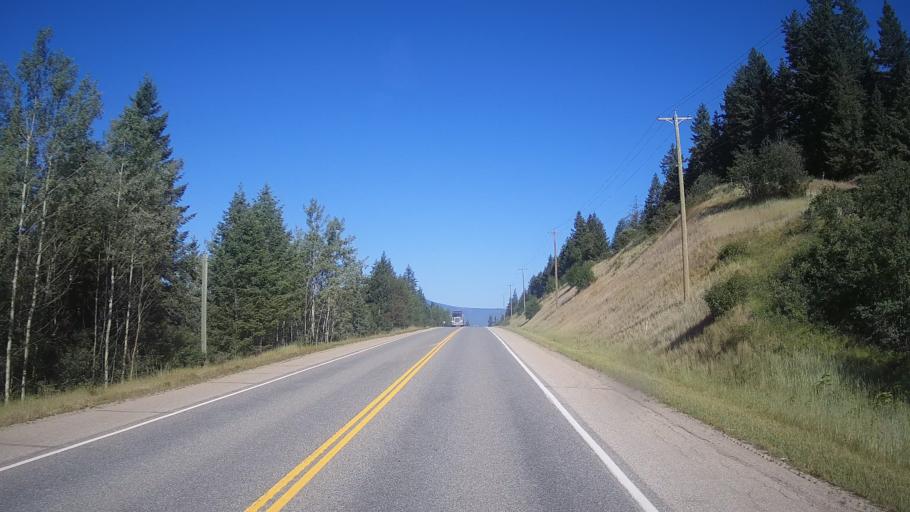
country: CA
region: British Columbia
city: Chase
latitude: 51.6014
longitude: -119.8894
